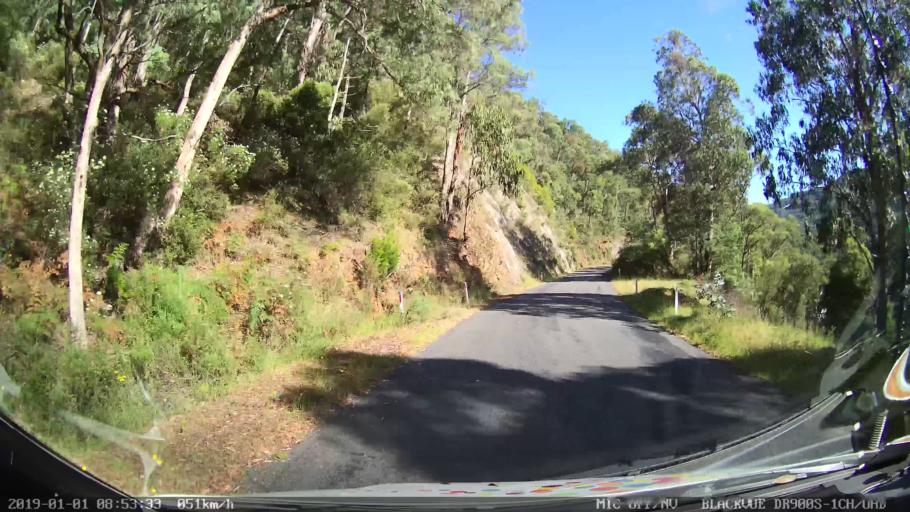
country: AU
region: New South Wales
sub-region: Snowy River
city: Jindabyne
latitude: -36.2650
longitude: 148.1901
